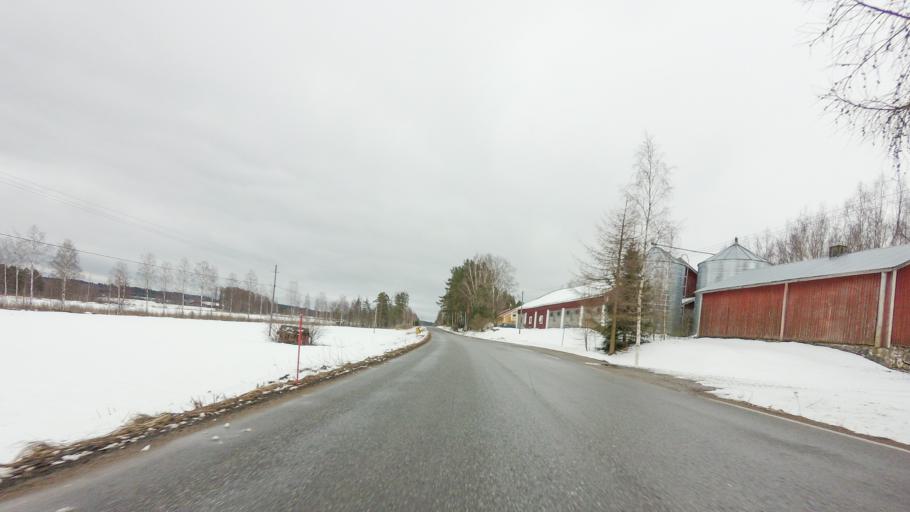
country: FI
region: Southern Savonia
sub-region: Savonlinna
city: Savonlinna
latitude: 61.9590
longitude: 28.8326
